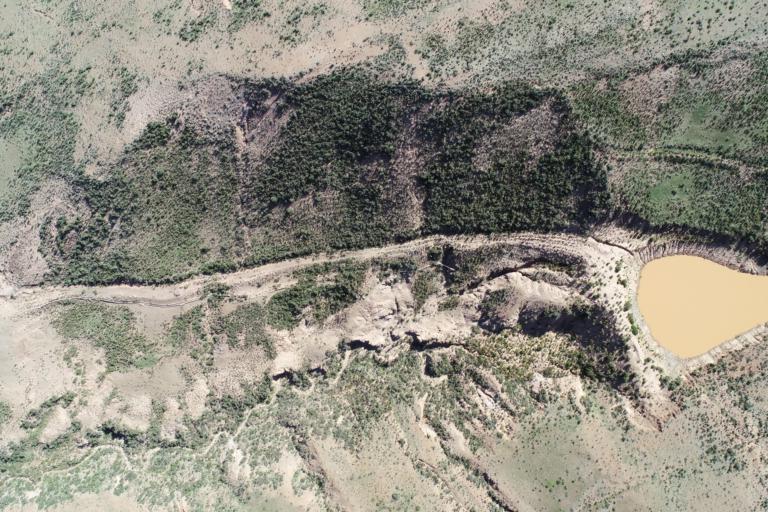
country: BO
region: La Paz
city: Curahuara de Carangas
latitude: -17.3032
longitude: -68.4863
